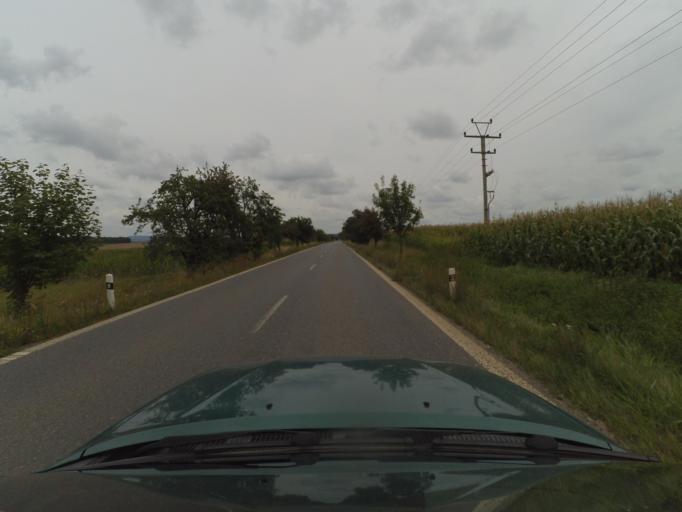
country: CZ
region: Central Bohemia
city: Rakovnik
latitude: 50.0795
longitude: 13.7168
